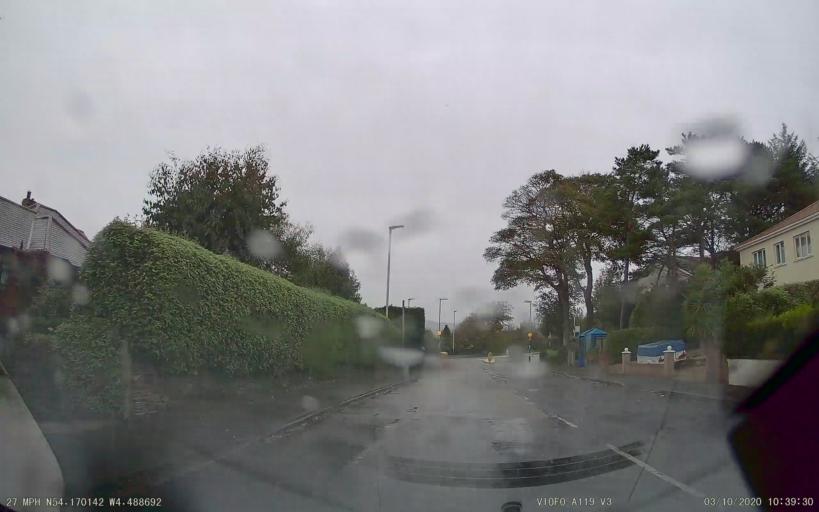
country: IM
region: Douglas
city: Douglas
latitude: 54.1701
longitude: -4.4886
